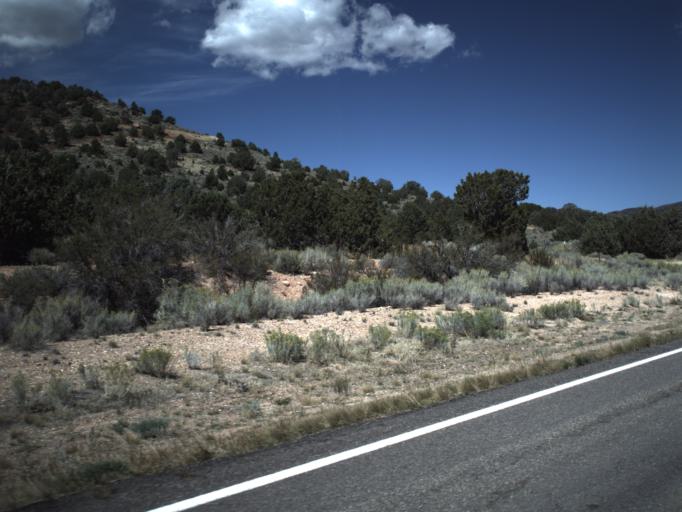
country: US
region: Utah
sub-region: Washington County
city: Enterprise
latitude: 37.4056
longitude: -113.6367
